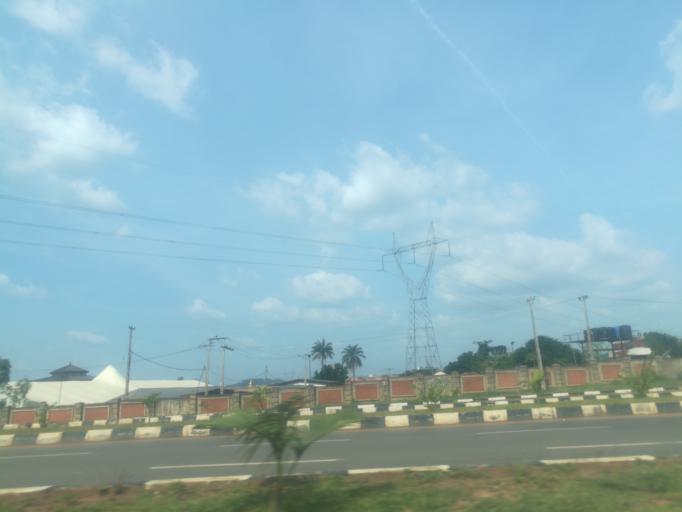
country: NG
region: Ogun
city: Abeokuta
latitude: 7.1246
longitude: 3.3590
